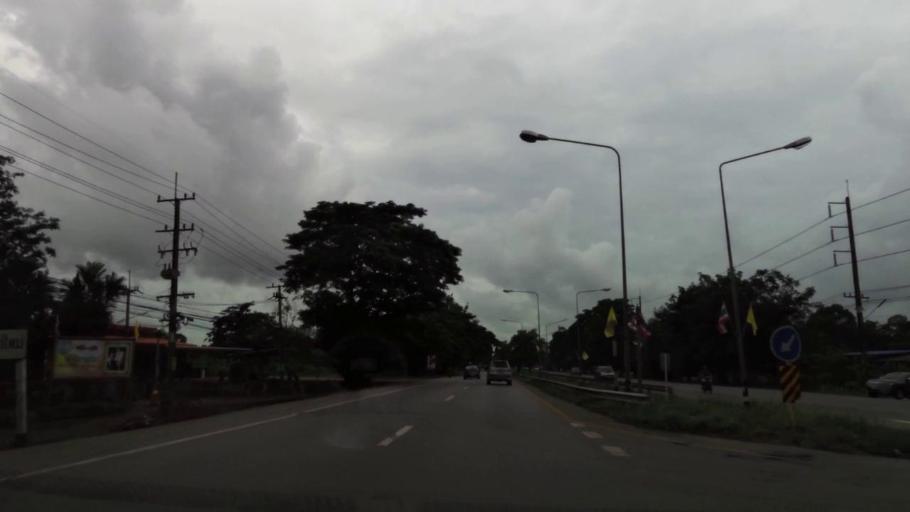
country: TH
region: Chanthaburi
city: Tha Mai
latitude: 12.6495
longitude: 102.0324
